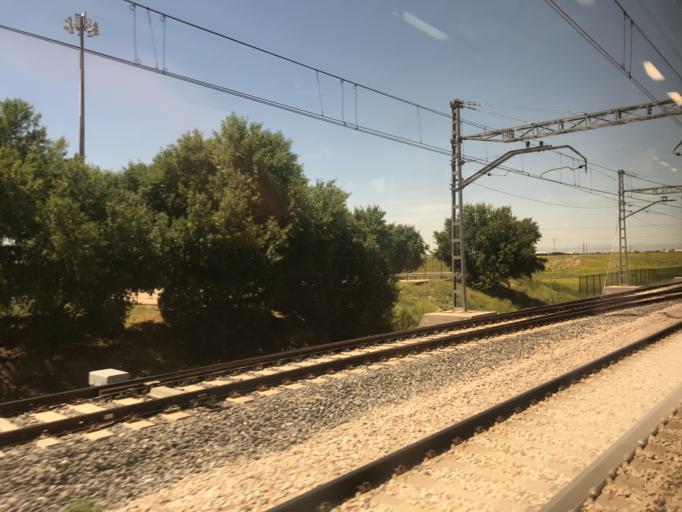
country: ES
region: Madrid
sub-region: Provincia de Madrid
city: Pinto
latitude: 40.2586
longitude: -3.7044
